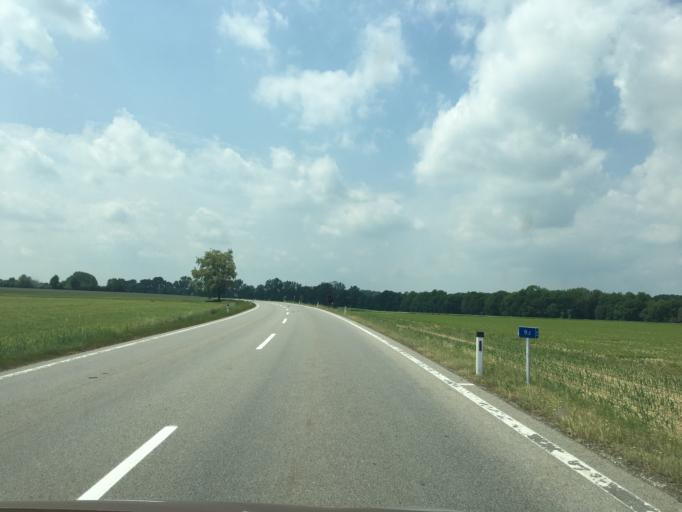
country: DE
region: Bavaria
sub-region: Lower Bavaria
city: Bad Fussing
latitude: 48.3012
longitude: 13.3225
